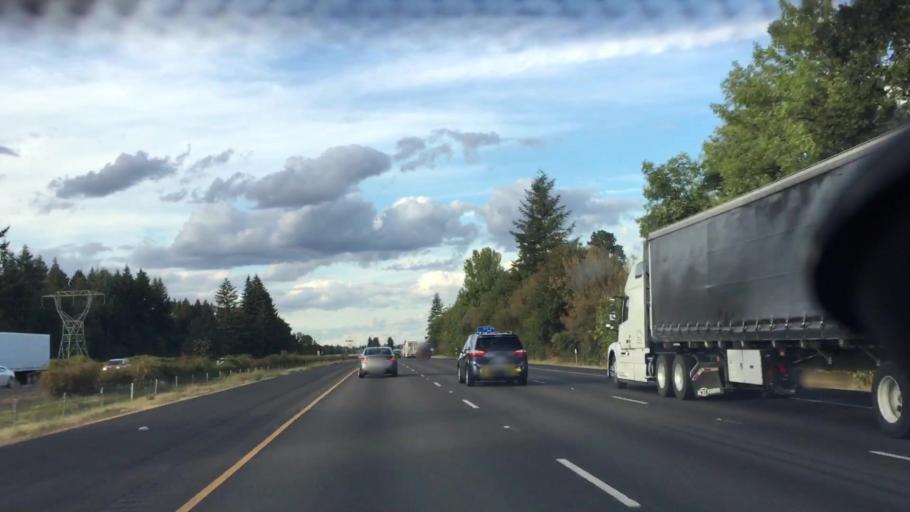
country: US
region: Oregon
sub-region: Marion County
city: Hubbard
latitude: 45.2205
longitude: -122.8181
